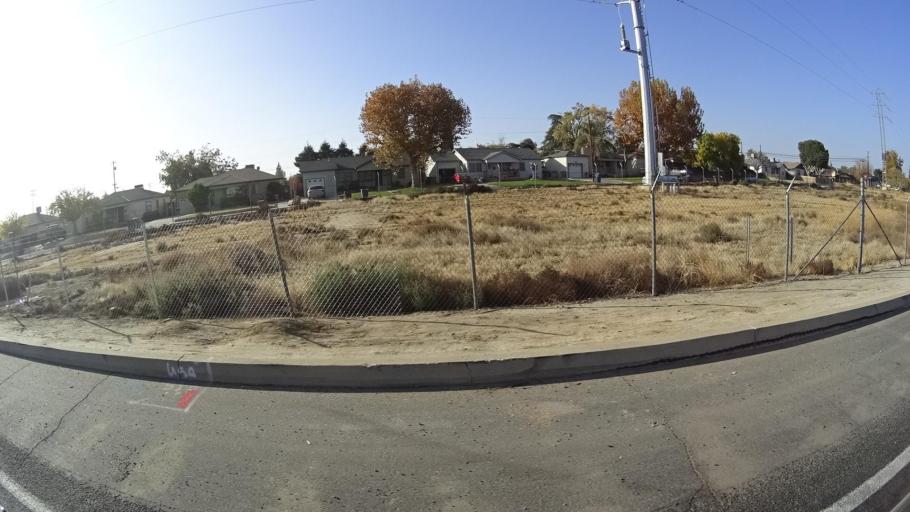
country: US
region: California
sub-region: Kern County
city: Oildale
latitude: 35.4256
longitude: -119.0128
